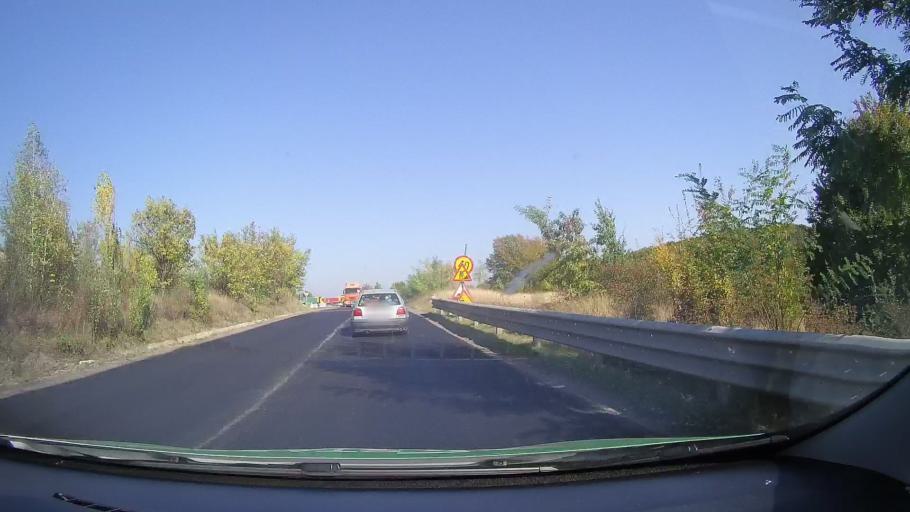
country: RO
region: Timis
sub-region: Comuna Curtea
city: Curtea
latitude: 45.8529
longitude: 22.3264
